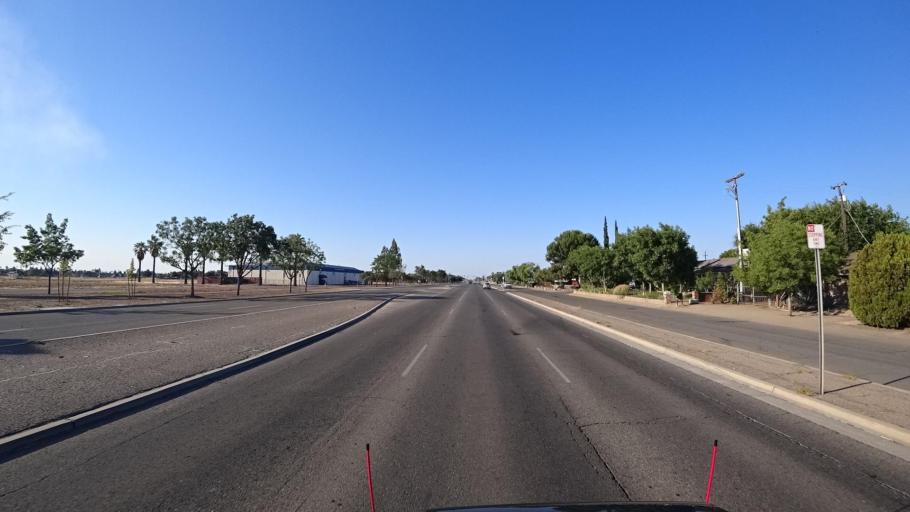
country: US
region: California
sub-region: Fresno County
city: Tarpey Village
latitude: 36.7902
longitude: -119.7004
